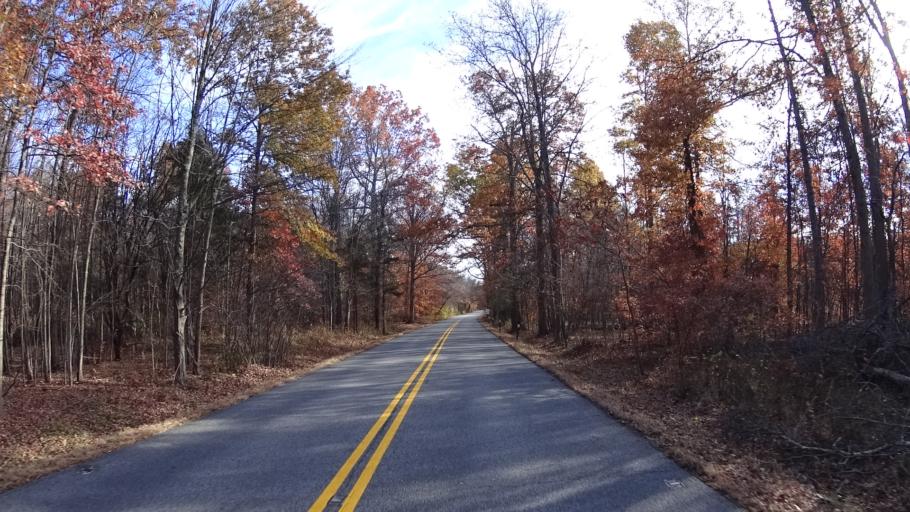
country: US
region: New Jersey
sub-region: Union County
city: Berkeley Heights
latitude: 40.7265
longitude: -74.4947
